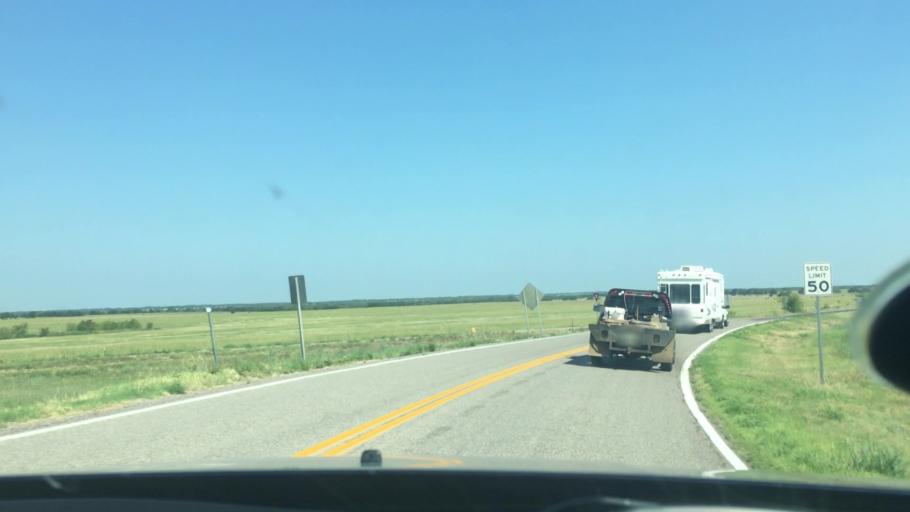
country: US
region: Oklahoma
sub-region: Johnston County
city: Tishomingo
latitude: 34.1439
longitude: -96.5039
